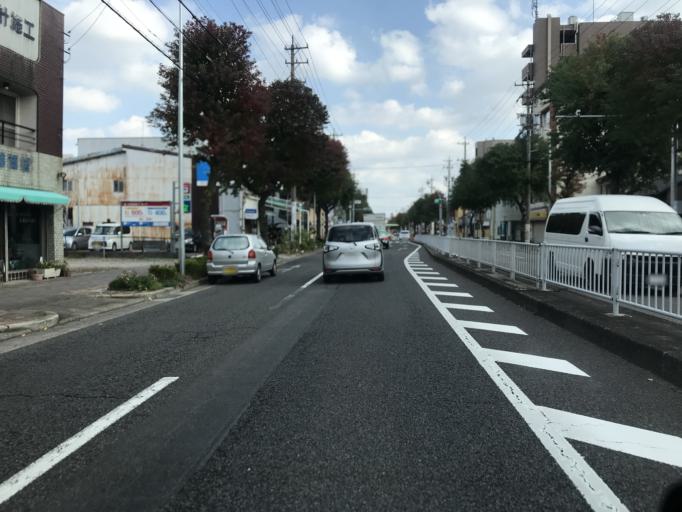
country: JP
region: Aichi
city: Nagoya-shi
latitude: 35.1777
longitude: 136.8578
